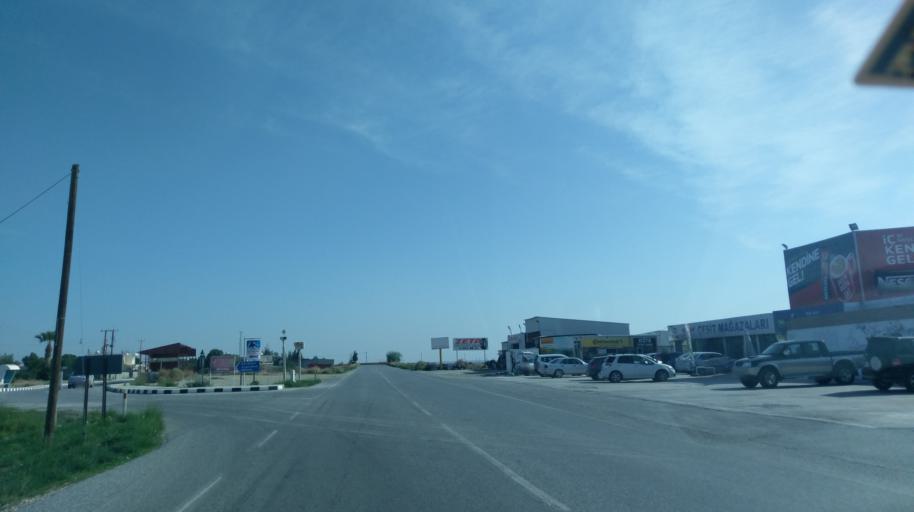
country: CY
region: Ammochostos
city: Lefkonoiko
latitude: 35.2423
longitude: 33.5977
